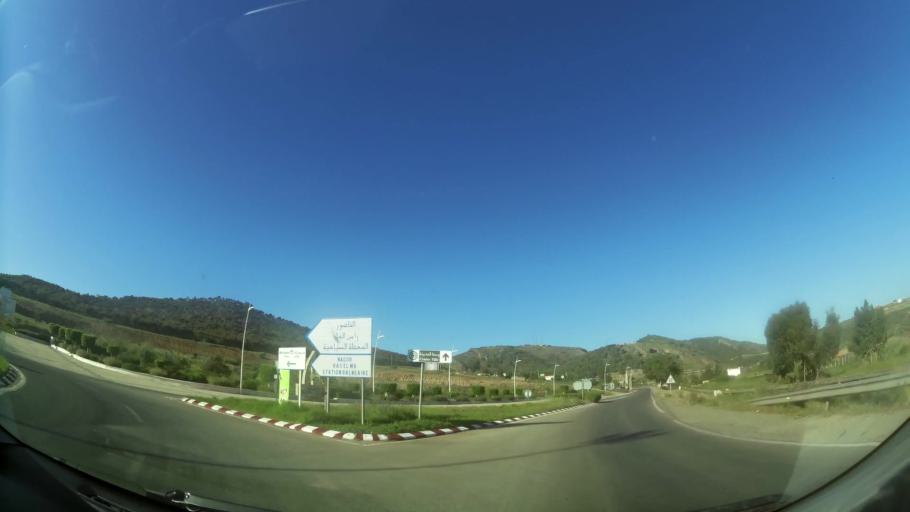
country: MA
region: Oriental
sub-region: Berkane-Taourirt
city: Madagh
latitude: 35.0505
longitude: -2.2185
